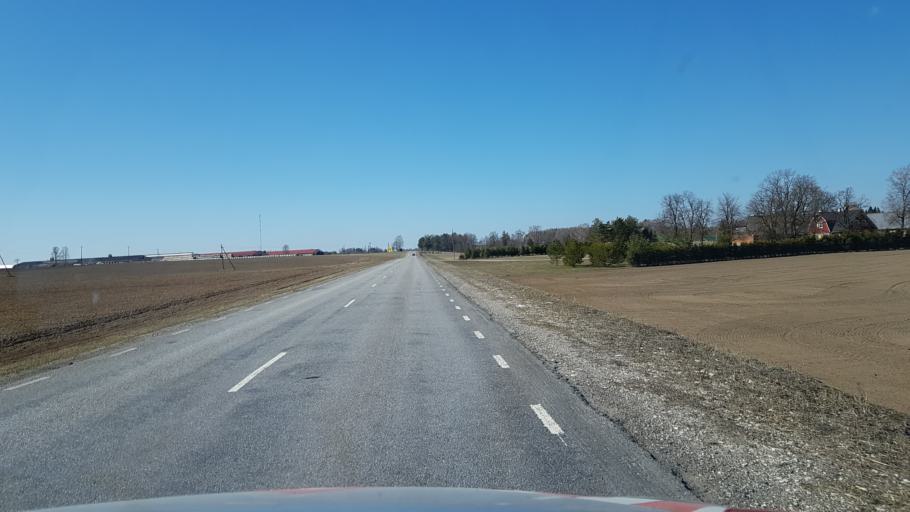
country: EE
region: Laeaene-Virumaa
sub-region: Vaeike-Maarja vald
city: Vaike-Maarja
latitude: 59.1615
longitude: 26.1897
